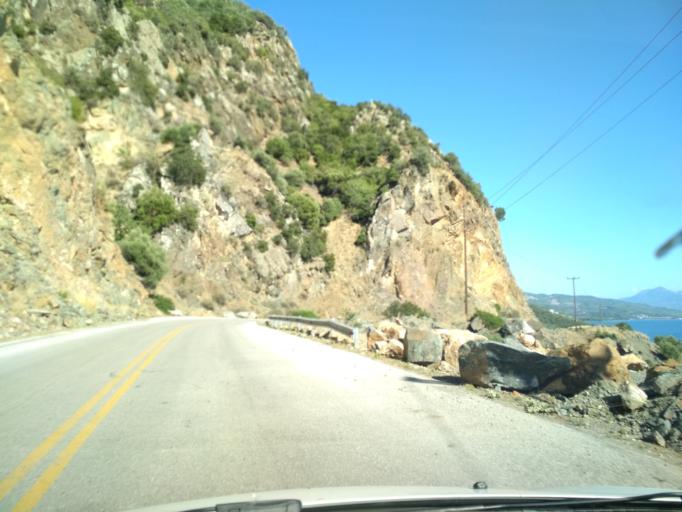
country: GR
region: Central Greece
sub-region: Nomos Evvoias
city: Roviai
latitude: 38.8468
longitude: 23.1593
